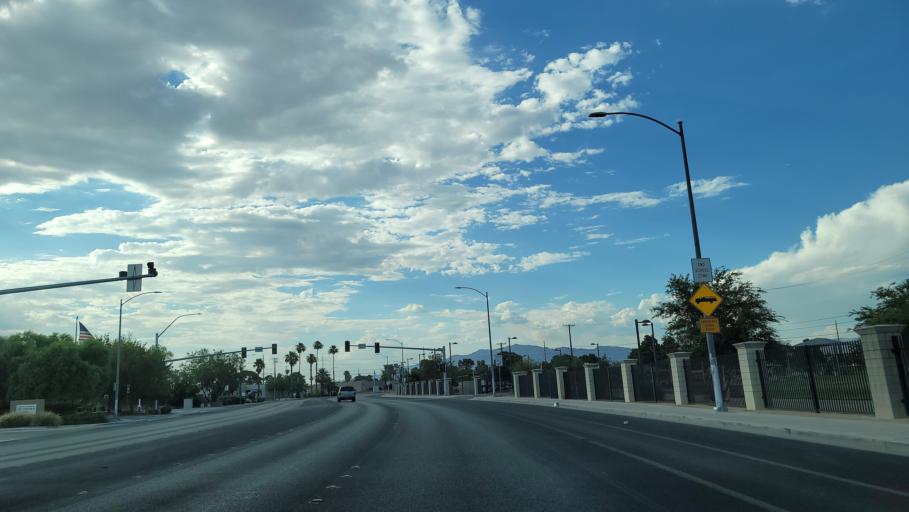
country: US
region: Nevada
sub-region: Clark County
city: North Las Vegas
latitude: 36.1776
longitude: -115.1059
